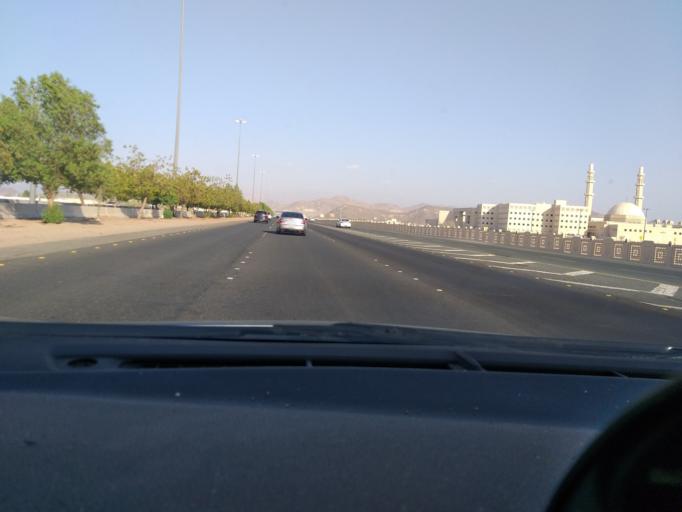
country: SA
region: Makkah
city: Mecca
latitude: 21.3348
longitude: 39.9495
